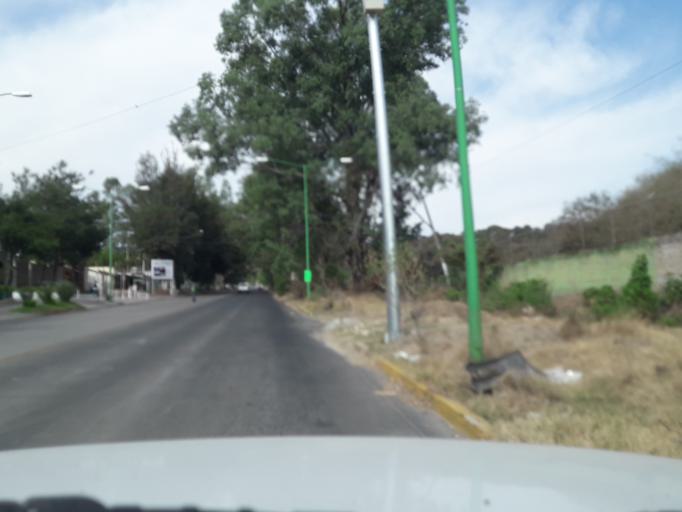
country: MX
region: Jalisco
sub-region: Tlajomulco de Zuniga
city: Palomar
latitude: 20.6179
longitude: -103.4832
